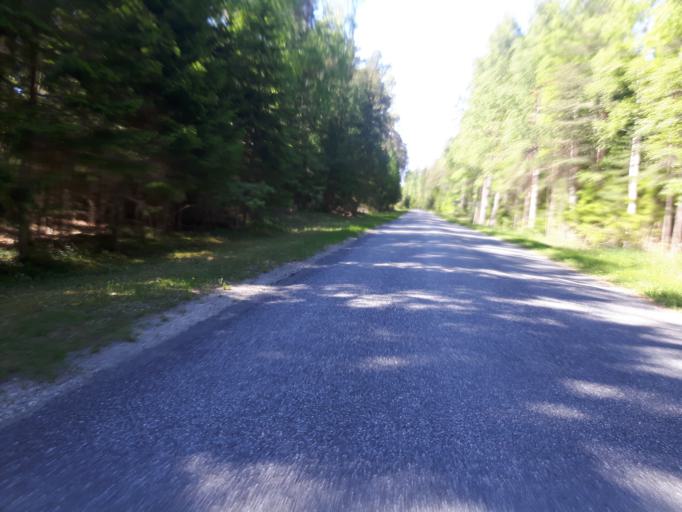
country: EE
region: Laeaene-Virumaa
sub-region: Haljala vald
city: Haljala
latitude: 59.5734
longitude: 26.2809
